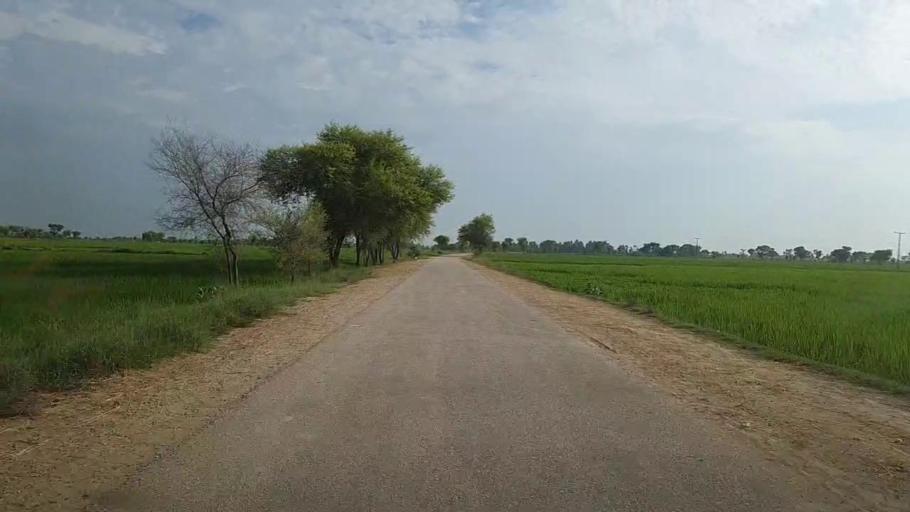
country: PK
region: Sindh
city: Thul
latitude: 28.2626
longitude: 68.8593
